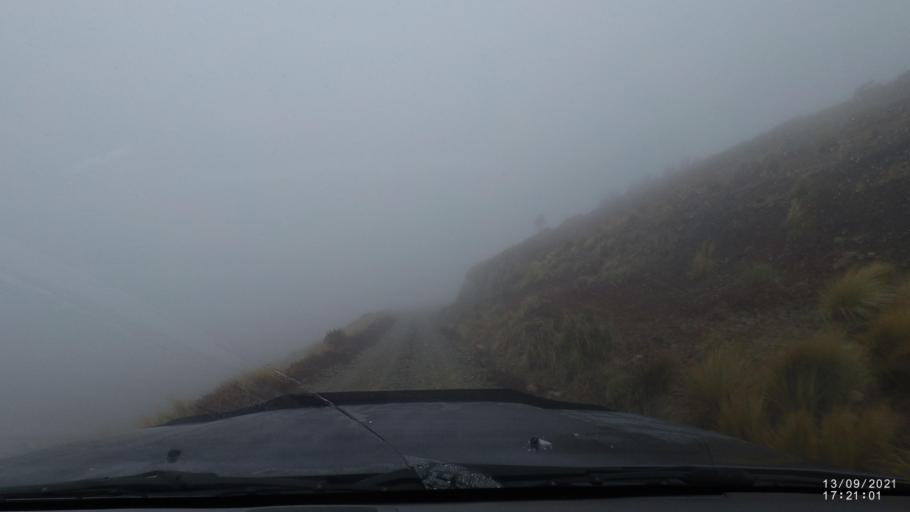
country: BO
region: Cochabamba
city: Colomi
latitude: -17.3519
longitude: -65.7671
